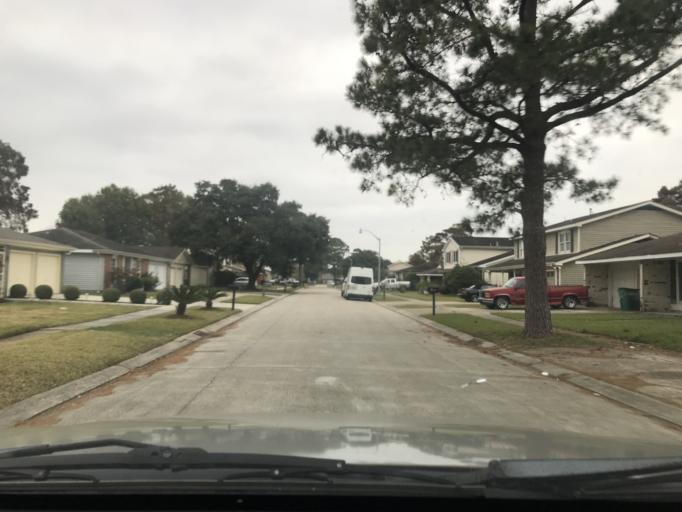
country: US
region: Louisiana
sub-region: Jefferson Parish
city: Woodmere
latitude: 29.8624
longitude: -90.0757
